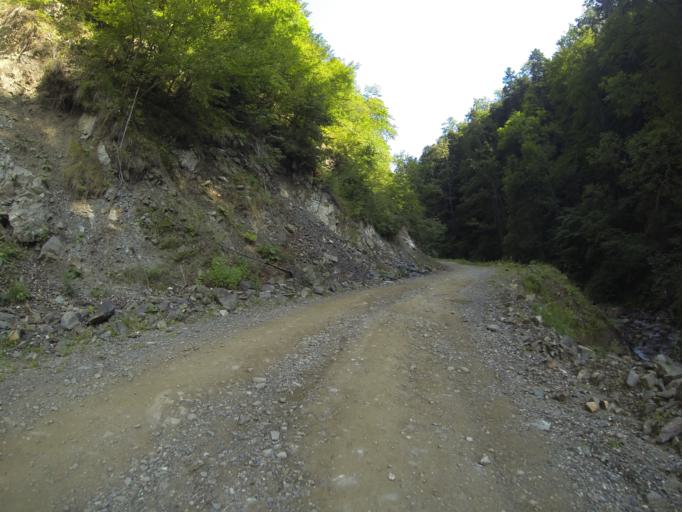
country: RO
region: Valcea
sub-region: Comuna Costesti
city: Bistrita
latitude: 45.2382
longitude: 24.0019
